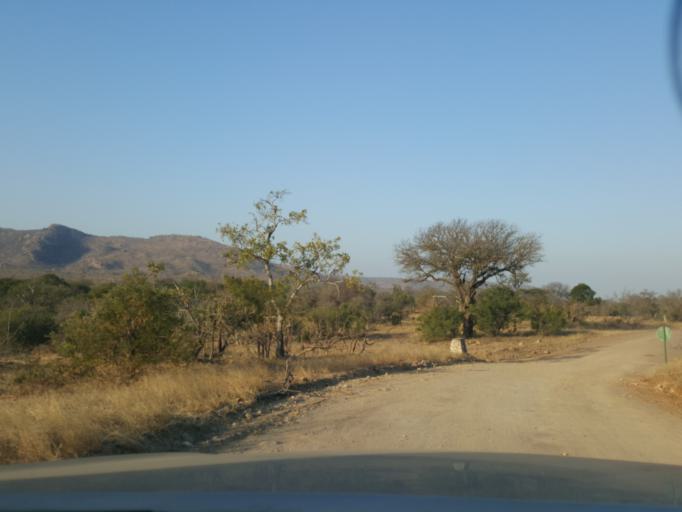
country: SZ
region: Hhohho
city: Ntfonjeni
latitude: -25.4283
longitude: 31.4424
